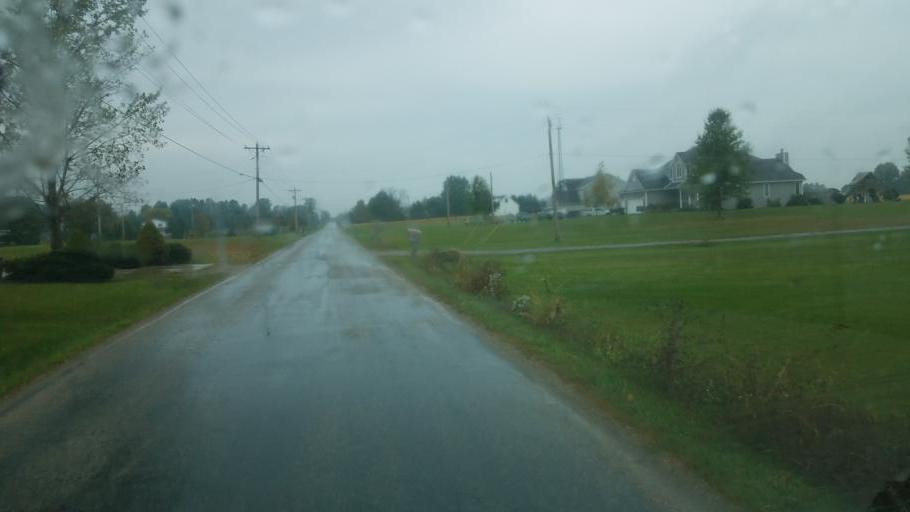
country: US
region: Ohio
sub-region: Ashland County
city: Ashland
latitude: 40.8145
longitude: -82.3423
